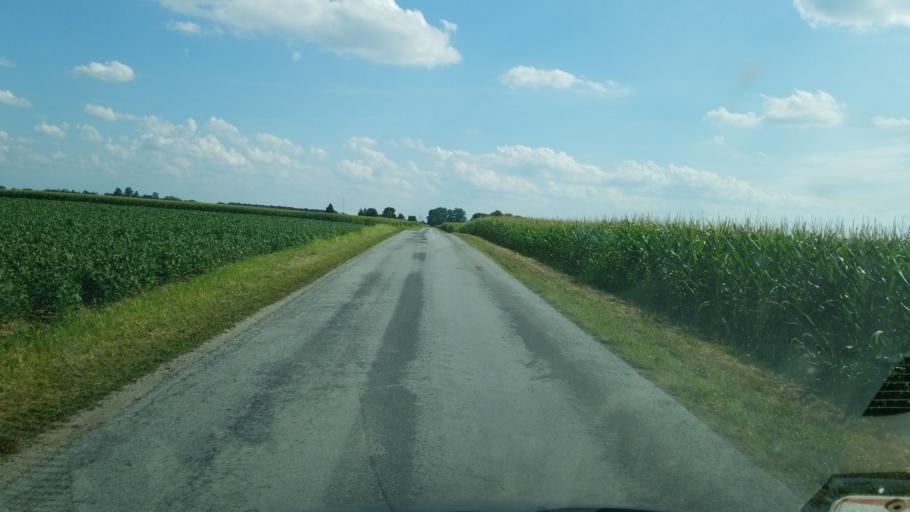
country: US
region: Ohio
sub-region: Marion County
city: Prospect
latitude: 40.5062
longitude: -83.2338
